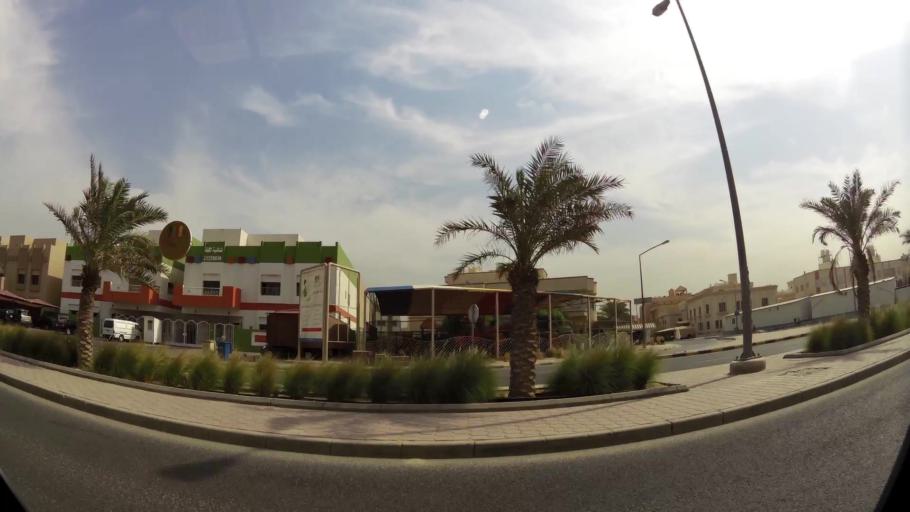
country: KW
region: Al Farwaniyah
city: Janub as Surrah
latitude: 29.2861
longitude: 48.0077
